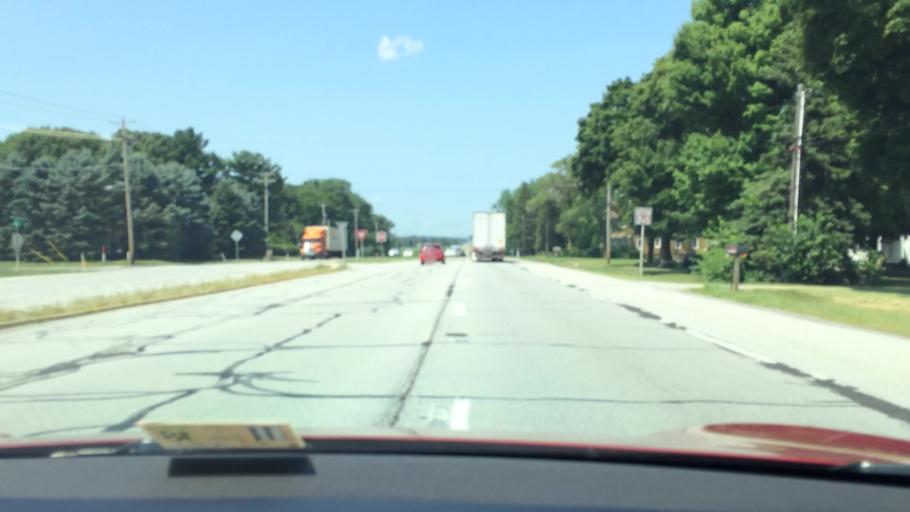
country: US
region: Indiana
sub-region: Saint Joseph County
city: New Carlisle
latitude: 41.6719
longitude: -86.3824
